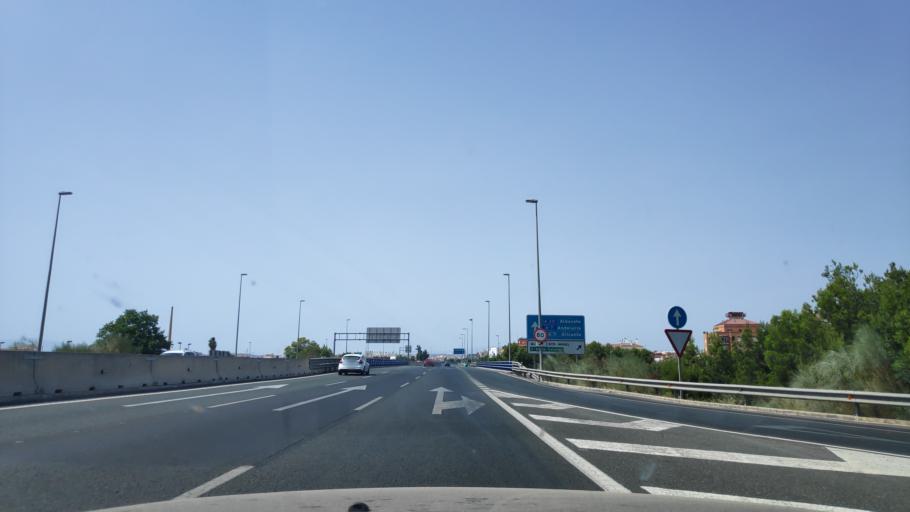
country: ES
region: Murcia
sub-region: Murcia
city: Murcia
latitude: 37.9656
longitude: -1.1364
